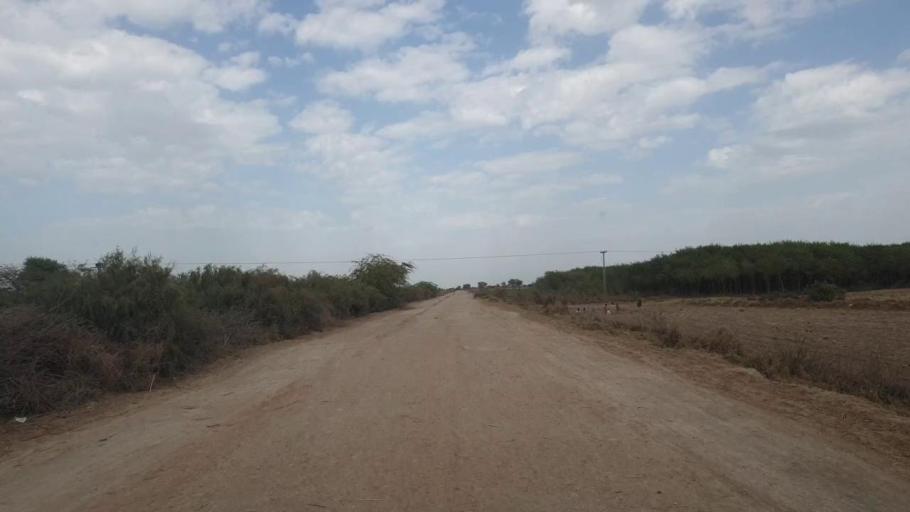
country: PK
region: Sindh
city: Hala
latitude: 25.9560
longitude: 68.4637
